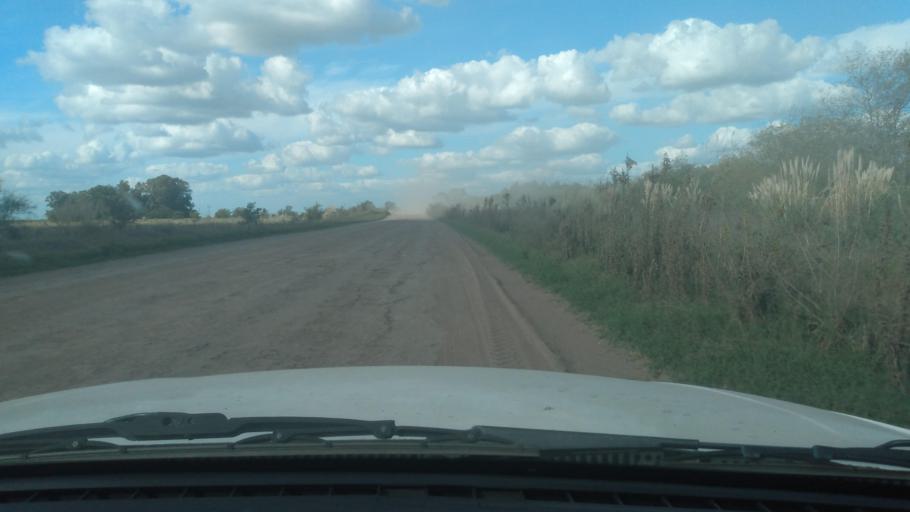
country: AR
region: Buenos Aires
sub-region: Partido de Navarro
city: Navarro
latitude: -35.0086
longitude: -59.3989
